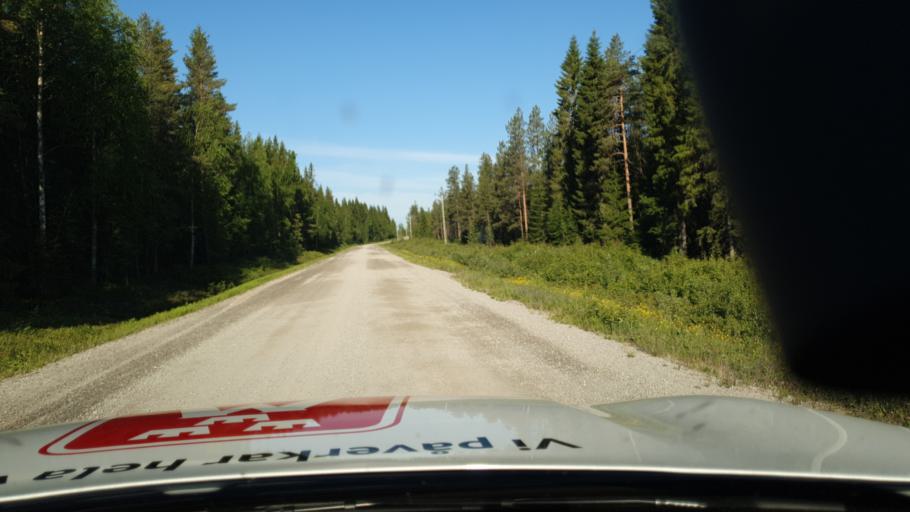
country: SE
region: Vaesterbotten
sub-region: Bjurholms Kommun
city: Bjurholm
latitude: 64.1850
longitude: 19.1745
